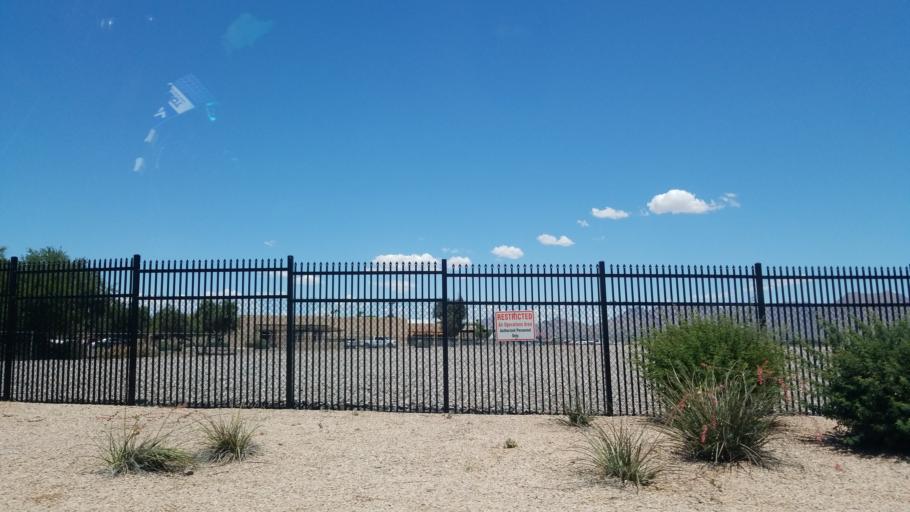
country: US
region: Arizona
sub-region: Maricopa County
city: Paradise Valley
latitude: 33.6123
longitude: -111.9240
